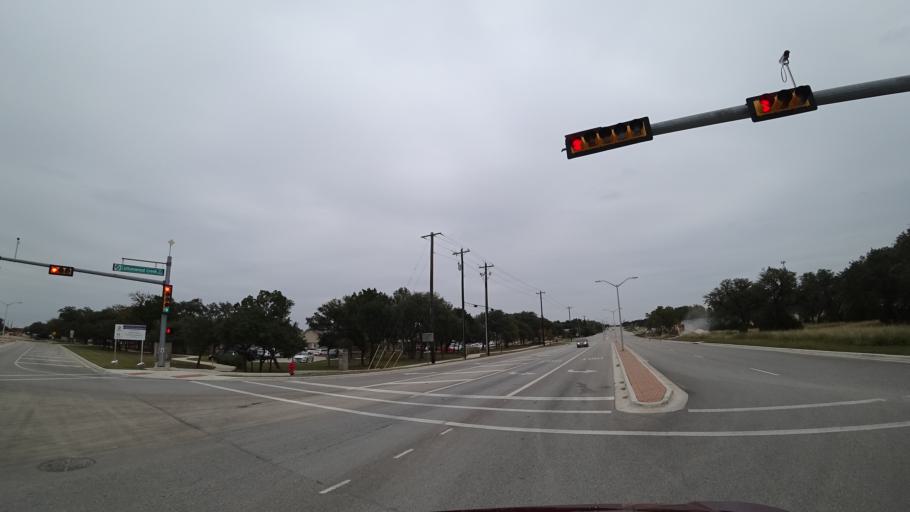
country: US
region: Texas
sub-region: Williamson County
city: Cedar Park
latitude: 30.5364
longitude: -97.8091
